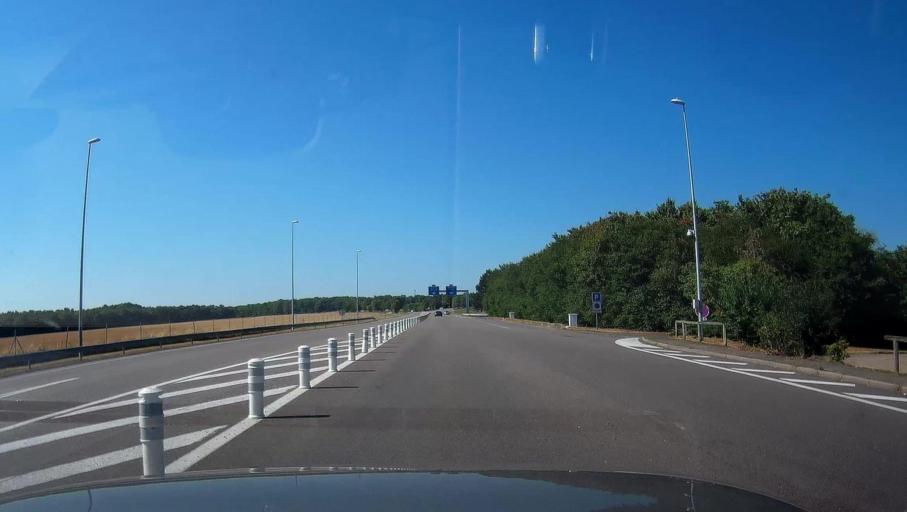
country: FR
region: Lorraine
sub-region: Departement de Meurthe-et-Moselle
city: Colombey-les-Belles
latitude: 48.5405
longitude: 5.9088
